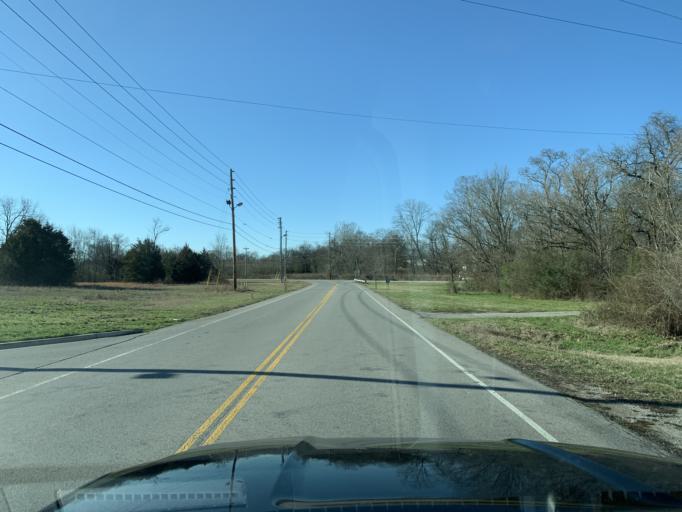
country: US
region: Tennessee
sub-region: Maury County
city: Spring Hill
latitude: 35.7494
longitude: -86.9222
